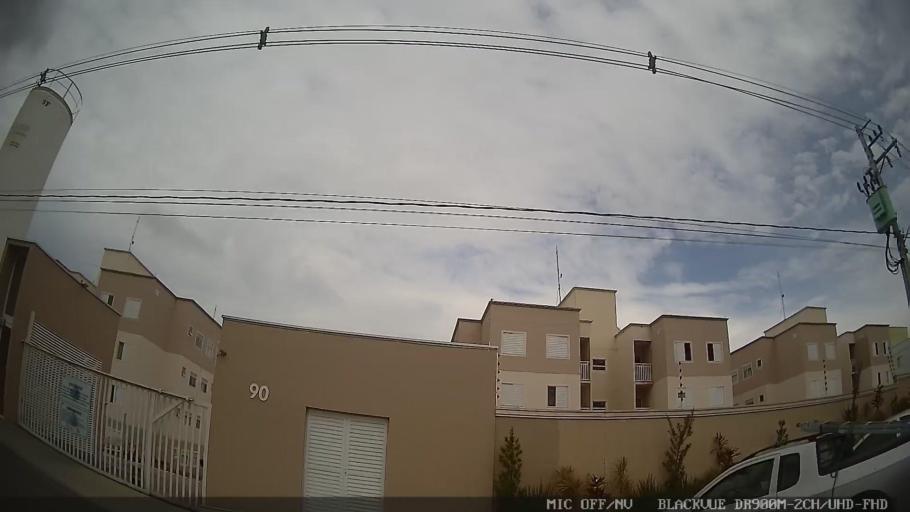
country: BR
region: Sao Paulo
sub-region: Salto
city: Salto
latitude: -23.1991
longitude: -47.2727
